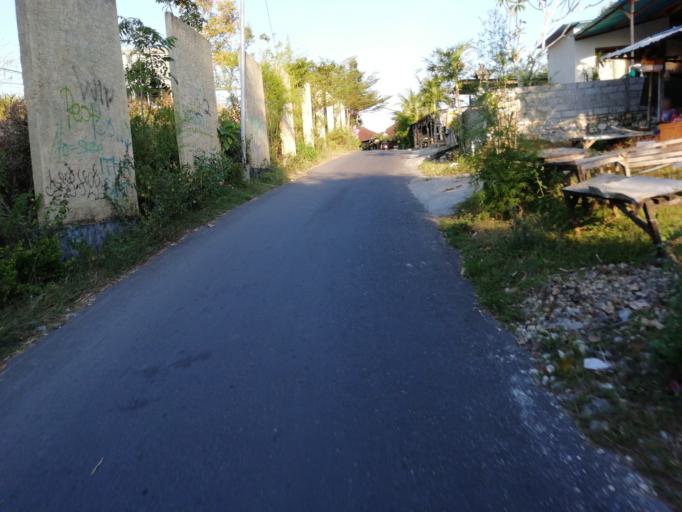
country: ID
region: Bali
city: Bualu
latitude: -8.8015
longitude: 115.1964
